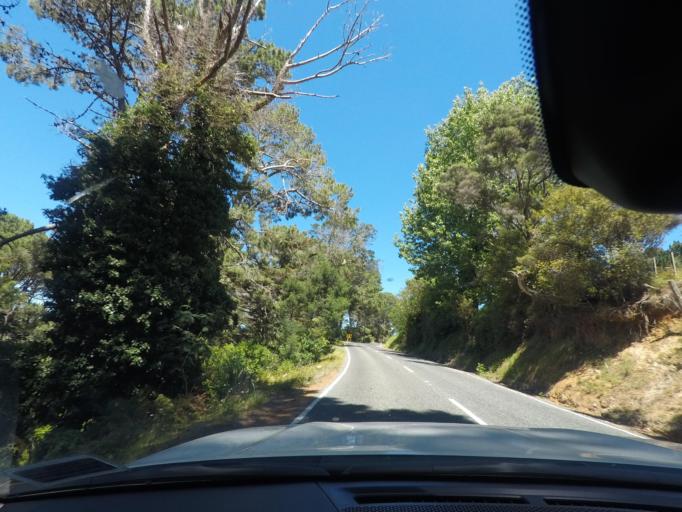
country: NZ
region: Auckland
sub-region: Auckland
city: Parakai
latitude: -36.5753
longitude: 174.3496
